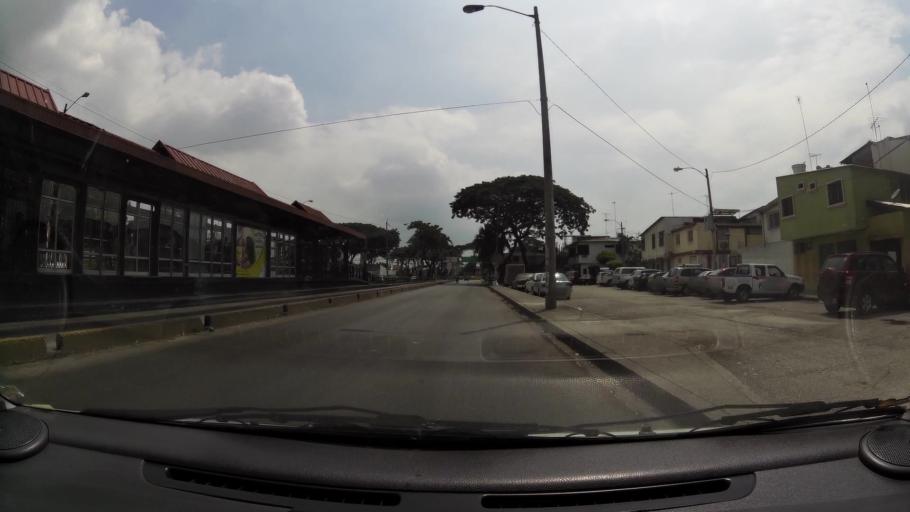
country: EC
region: Guayas
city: Guayaquil
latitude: -2.2411
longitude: -79.8910
